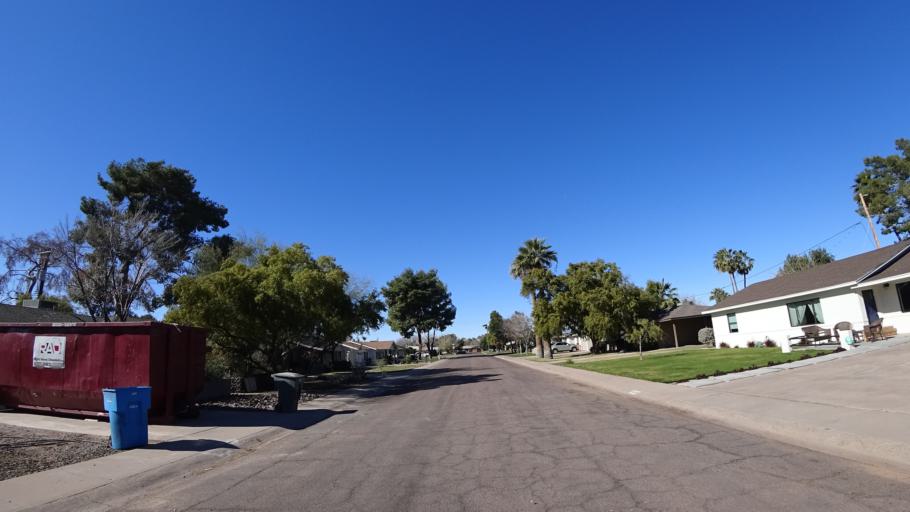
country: US
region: Arizona
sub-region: Maricopa County
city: Phoenix
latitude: 33.5143
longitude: -112.0595
